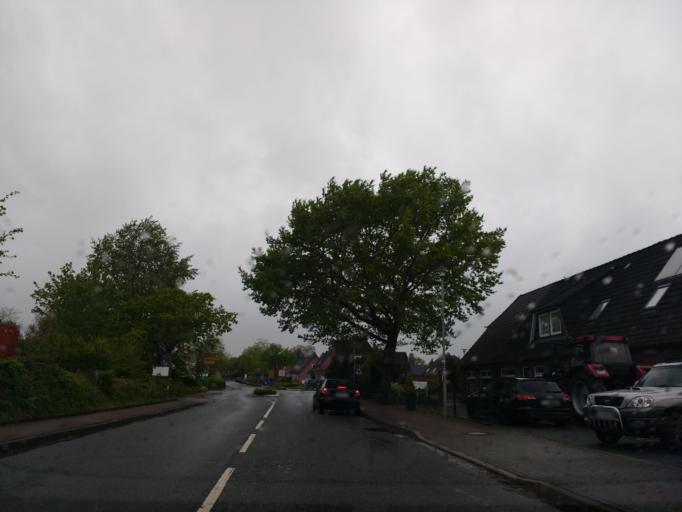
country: DE
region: Schleswig-Holstein
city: Damp
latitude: 54.5715
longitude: 9.9615
